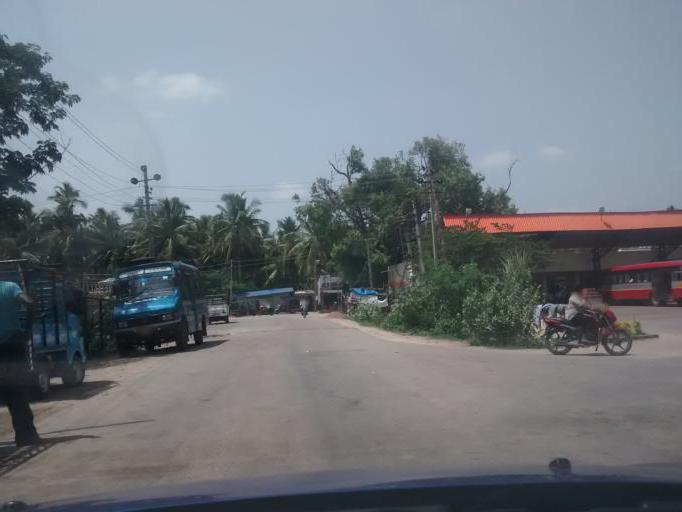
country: IN
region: Karnataka
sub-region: Hassan
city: Konanur
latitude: 12.5606
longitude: 76.2655
